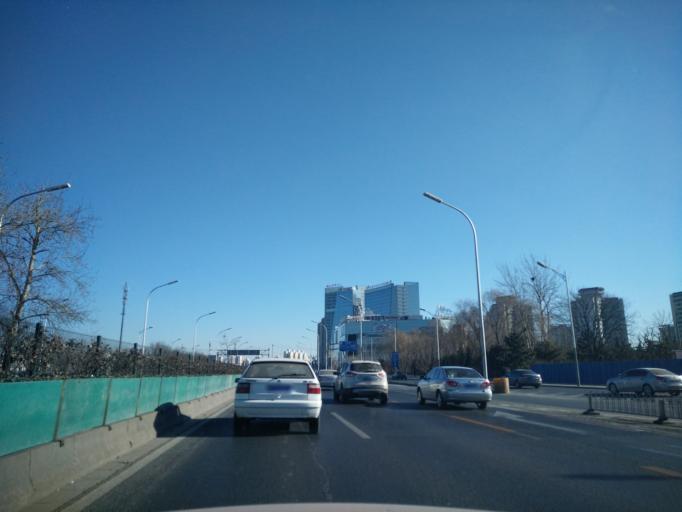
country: CN
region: Beijing
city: Baizhifang
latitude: 39.8527
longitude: 116.3555
